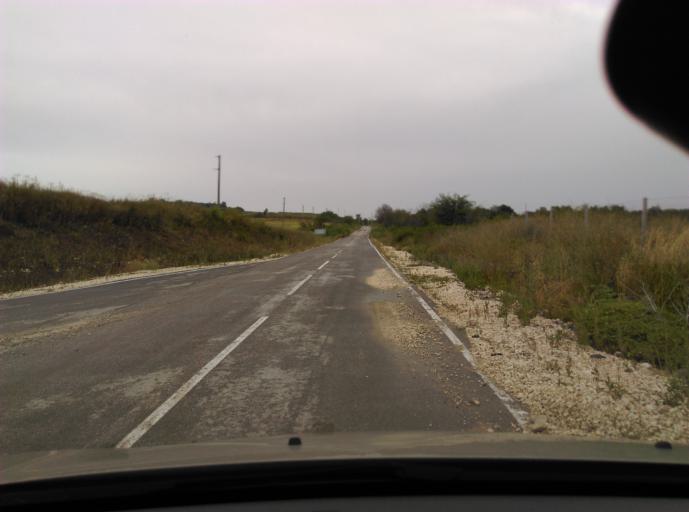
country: BG
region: Stara Zagora
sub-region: Obshtina Chirpan
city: Chirpan
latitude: 42.1067
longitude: 25.4186
